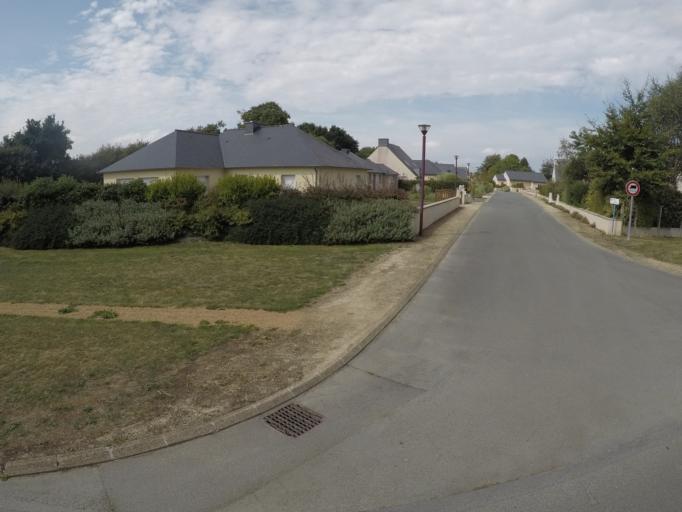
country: FR
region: Brittany
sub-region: Departement des Cotes-d'Armor
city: Goudelin
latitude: 48.5992
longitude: -3.0231
